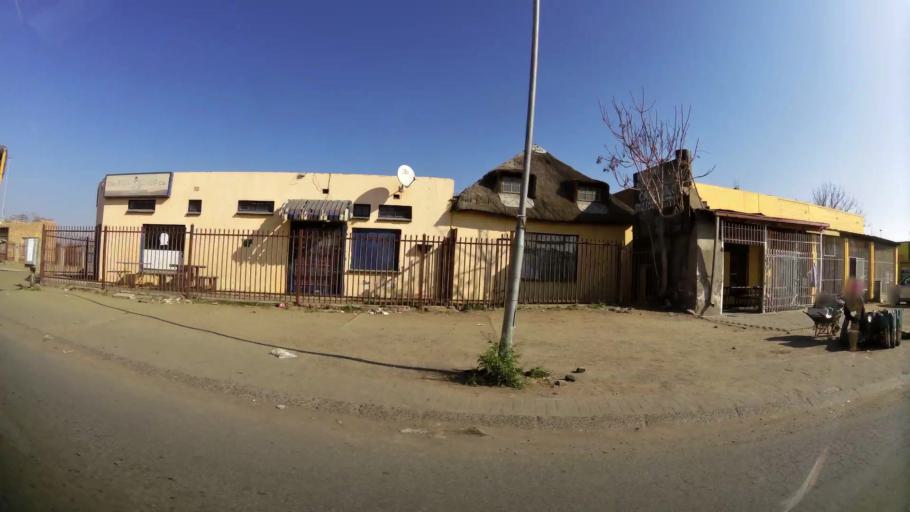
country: ZA
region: Orange Free State
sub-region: Mangaung Metropolitan Municipality
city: Bloemfontein
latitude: -29.1453
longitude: 26.2412
